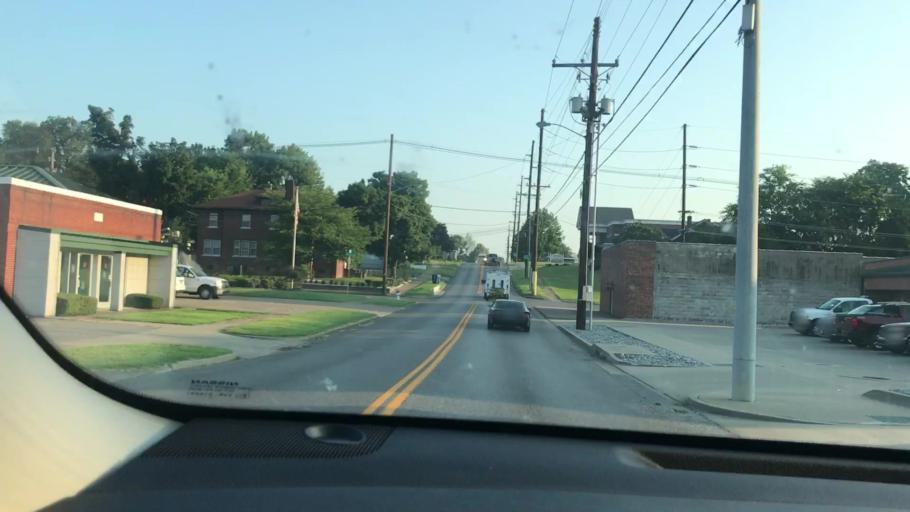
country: US
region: Kentucky
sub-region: Calloway County
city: Murray
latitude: 36.6120
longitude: -88.3021
